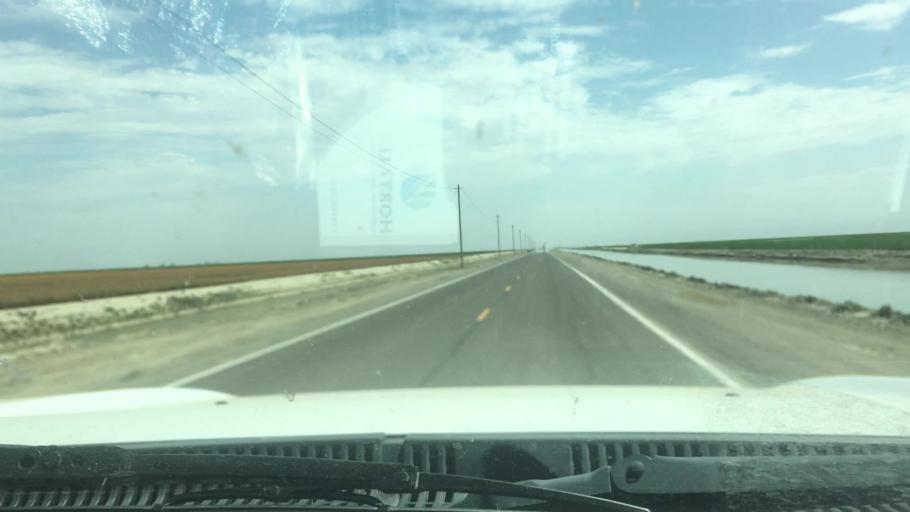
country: US
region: California
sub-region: Tulare County
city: Alpaugh
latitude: 35.9031
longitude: -119.5733
